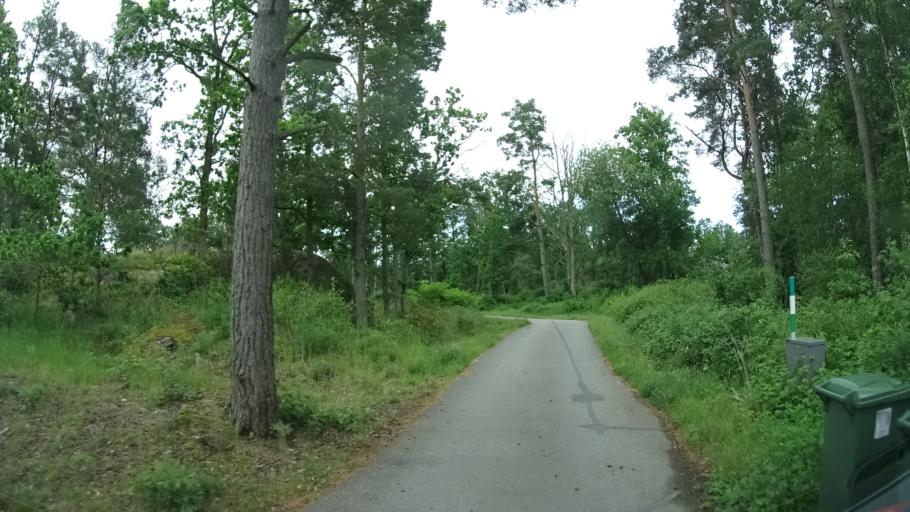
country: SE
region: Kalmar
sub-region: Oskarshamns Kommun
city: Oskarshamn
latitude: 57.2352
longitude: 16.5013
